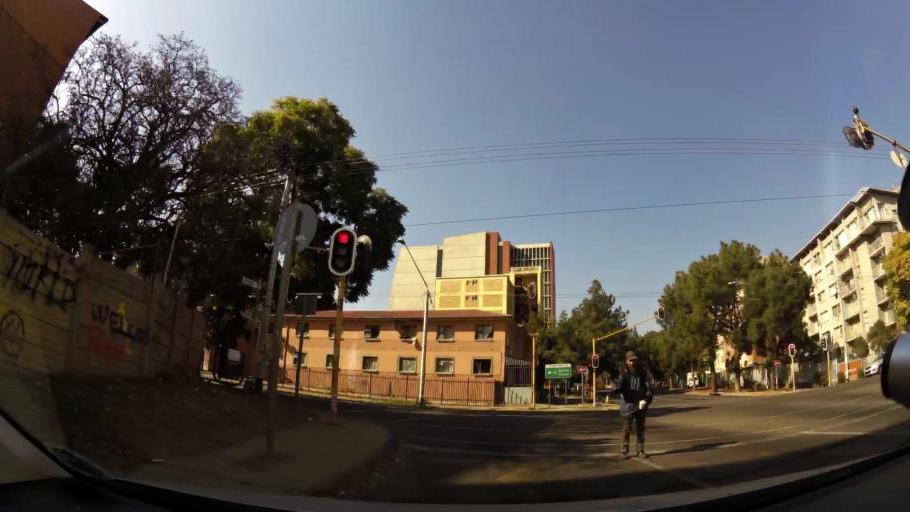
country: ZA
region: Gauteng
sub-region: City of Tshwane Metropolitan Municipality
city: Pretoria
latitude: -25.7408
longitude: 28.2034
